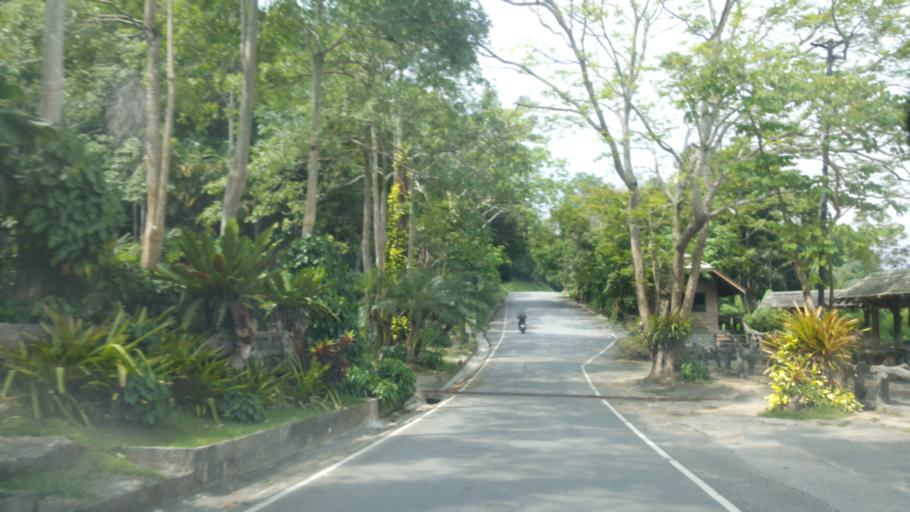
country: TH
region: Chon Buri
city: Ban Bueng
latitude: 13.2103
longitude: 101.0638
